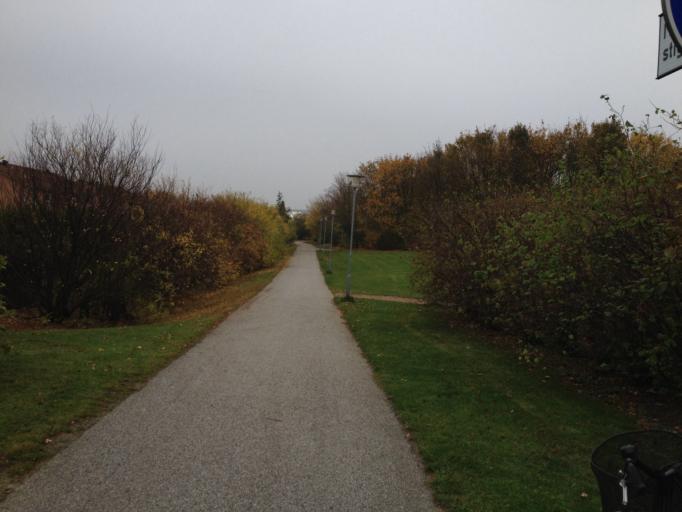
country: SE
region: Skane
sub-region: Burlovs Kommun
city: Arloev
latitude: 55.6055
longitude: 13.0523
